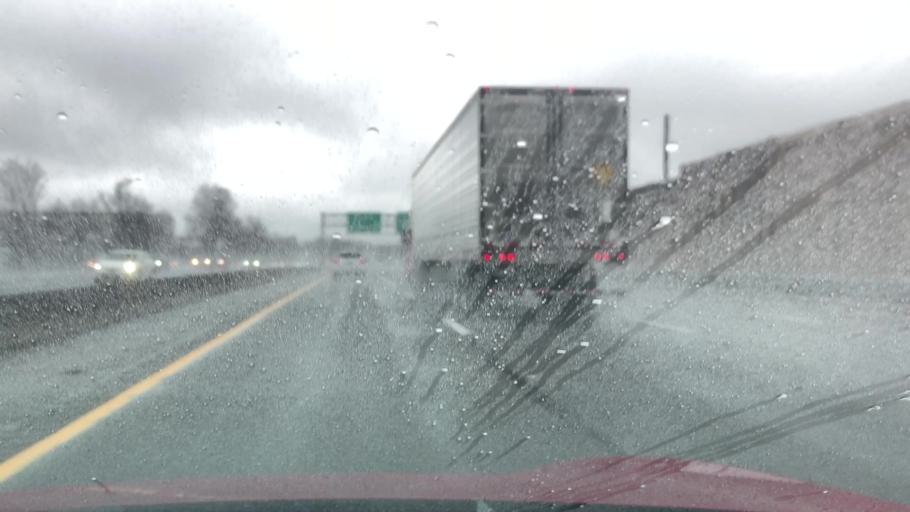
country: US
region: New Jersey
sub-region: Passaic County
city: Totowa
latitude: 40.8971
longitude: -74.2163
